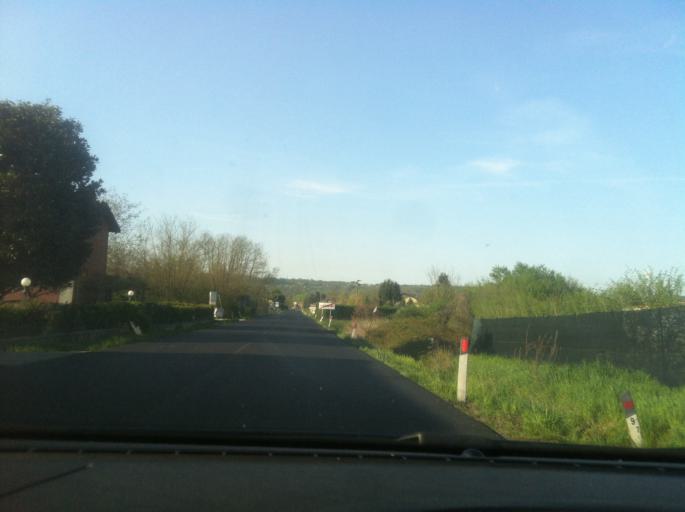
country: IT
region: Piedmont
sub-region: Provincia di Torino
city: Strambino
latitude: 45.3736
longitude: 7.8802
